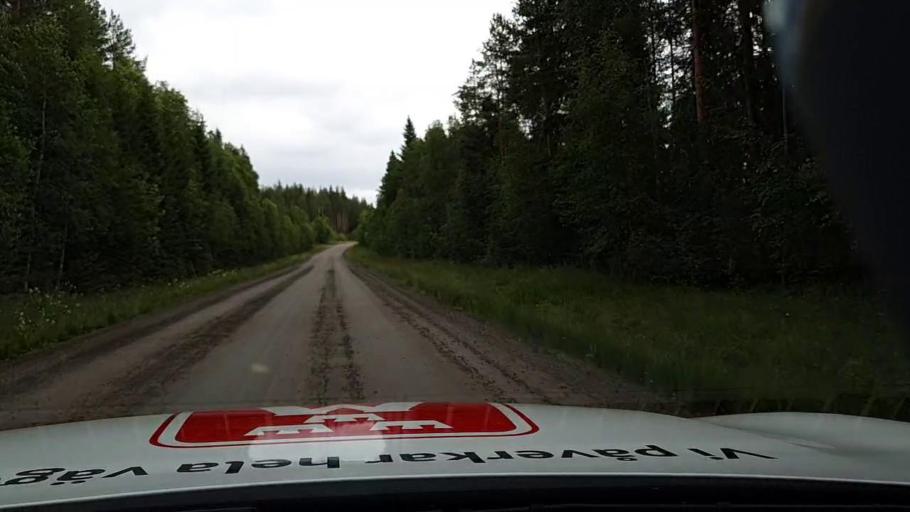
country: SE
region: Vaesternorrland
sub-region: Solleftea Kommun
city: As
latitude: 63.5109
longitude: 16.4023
